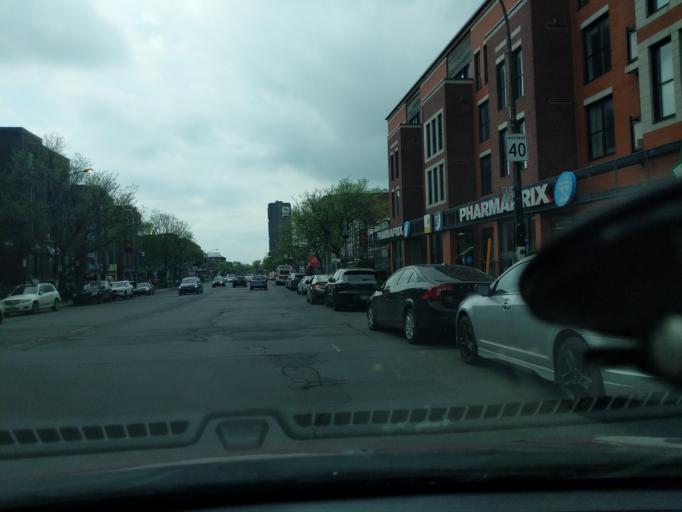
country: CA
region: Quebec
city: Saint-Raymond
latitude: 45.4862
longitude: -73.6270
